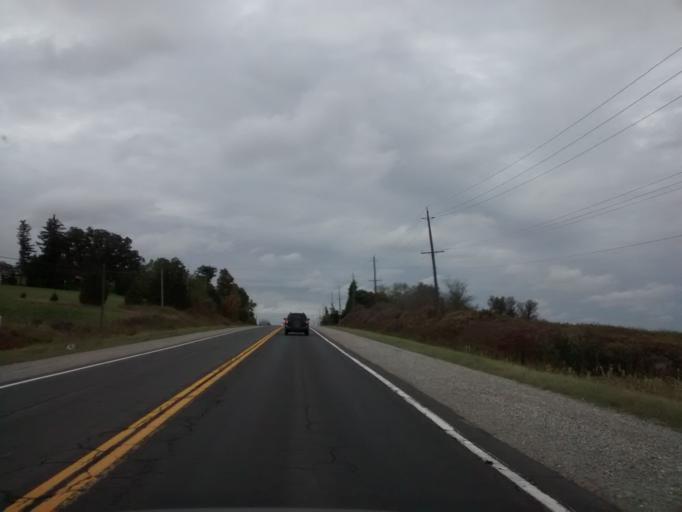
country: CA
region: Ontario
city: Ancaster
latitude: 43.0382
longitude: -79.9831
